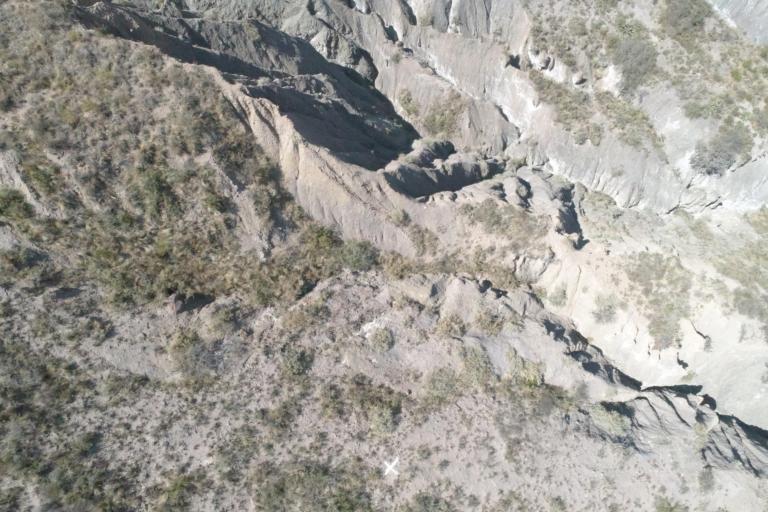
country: BO
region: La Paz
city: La Paz
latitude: -16.6229
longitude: -68.0395
